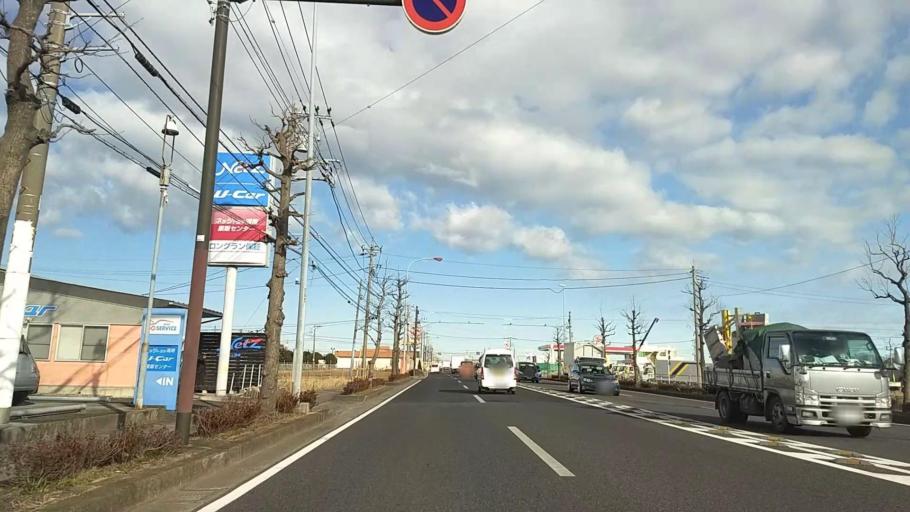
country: JP
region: Kanagawa
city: Atsugi
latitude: 35.3866
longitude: 139.3616
